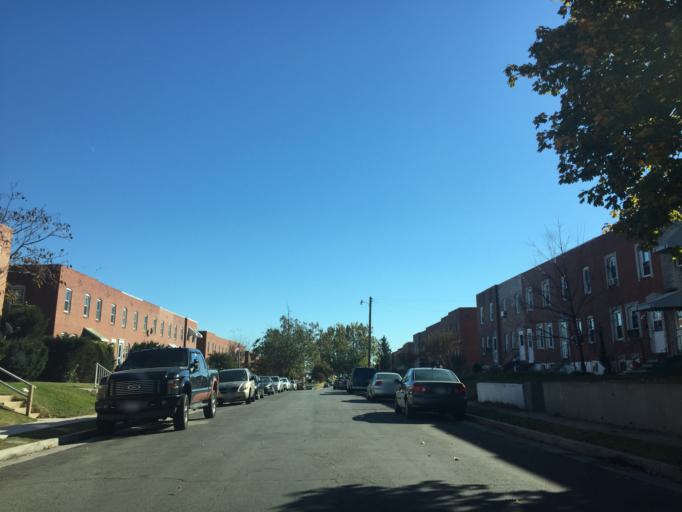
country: US
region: Maryland
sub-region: Baltimore County
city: Dundalk
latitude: 39.2570
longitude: -76.5140
